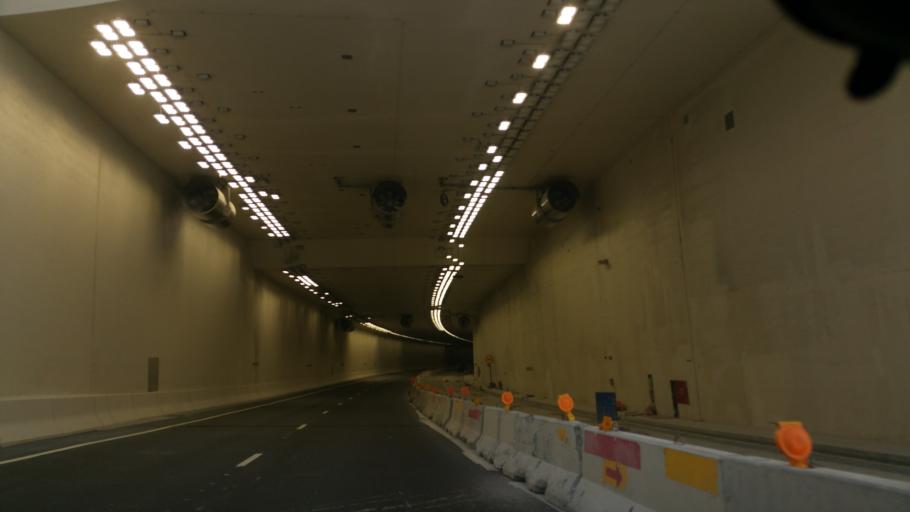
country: QA
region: Baladiyat Umm Salal
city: Umm Salal Muhammad
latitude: 25.4153
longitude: 51.5070
